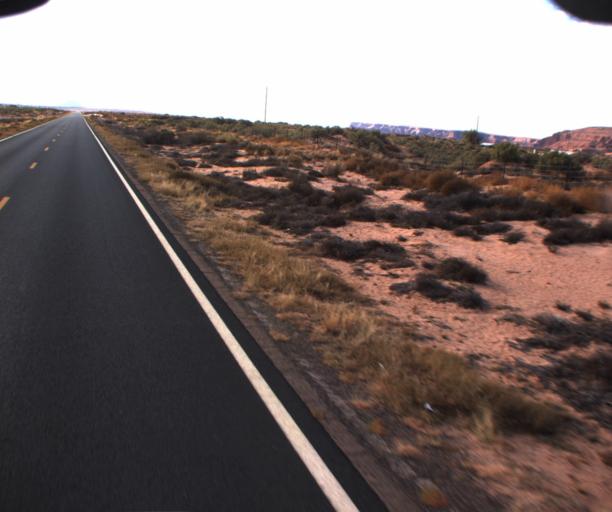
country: US
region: Arizona
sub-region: Apache County
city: Many Farms
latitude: 36.6562
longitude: -109.5941
